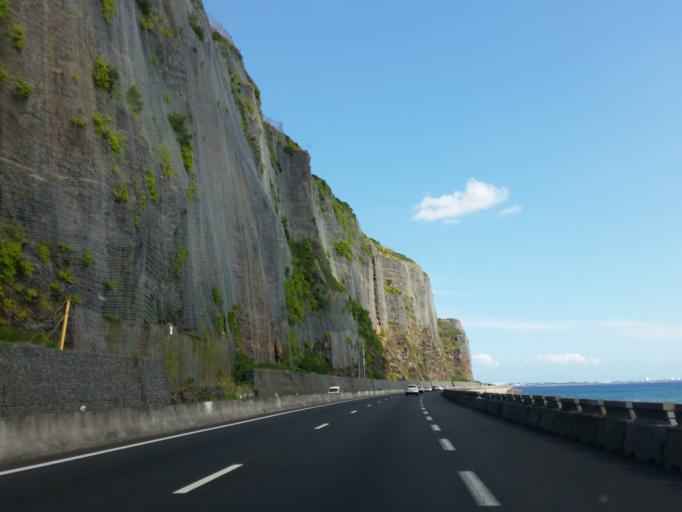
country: RE
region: Reunion
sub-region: Reunion
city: La Possession
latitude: -20.9076
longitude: 55.3609
